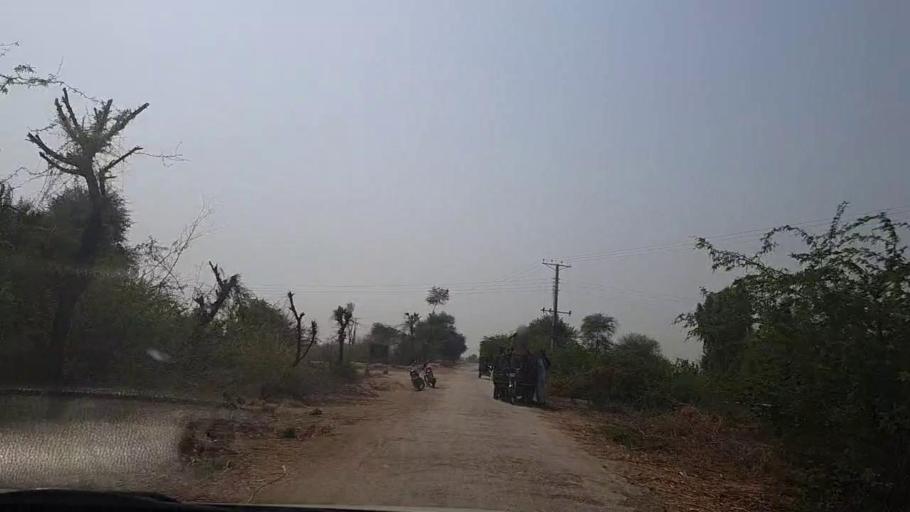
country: PK
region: Sindh
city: Pithoro
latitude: 25.5625
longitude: 69.2558
